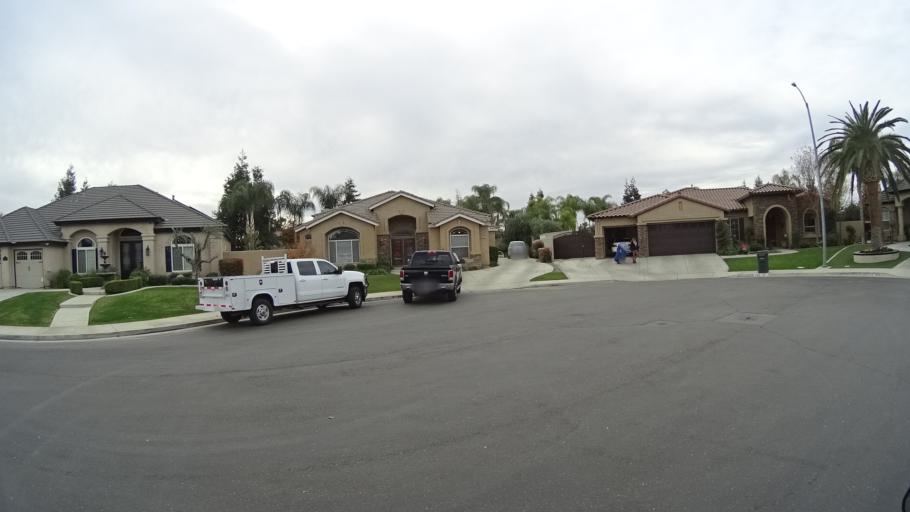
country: US
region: California
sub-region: Kern County
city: Rosedale
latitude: 35.4140
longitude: -119.1316
